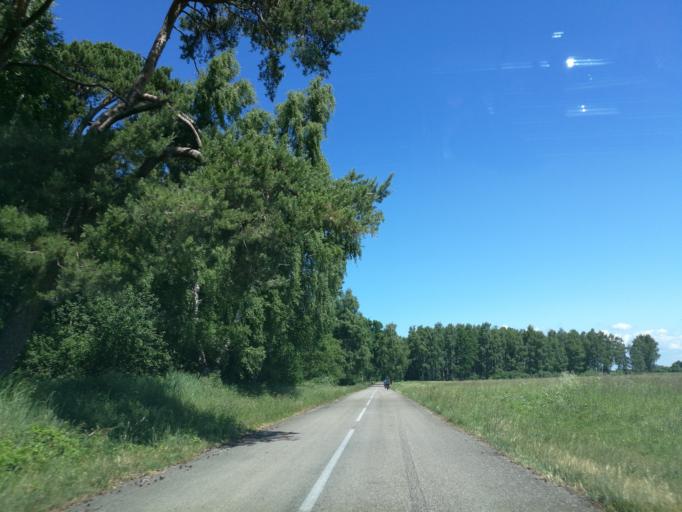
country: LT
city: Neringa
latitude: 55.3775
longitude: 21.2244
